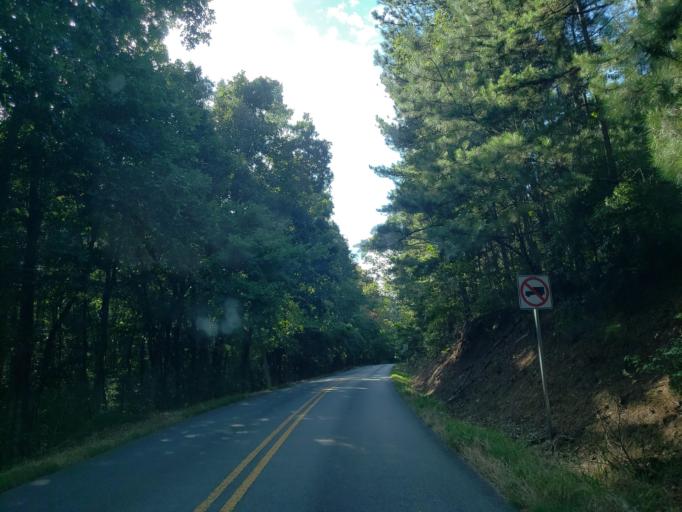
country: US
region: Georgia
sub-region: Floyd County
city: Rome
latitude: 34.2213
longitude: -85.1350
